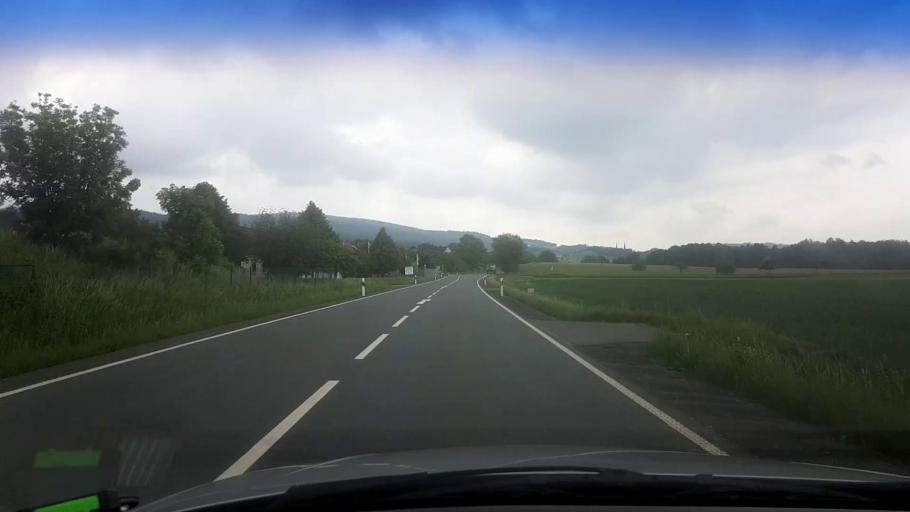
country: DE
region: Bavaria
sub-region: Upper Franconia
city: Goldkronach
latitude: 50.0103
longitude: 11.6751
